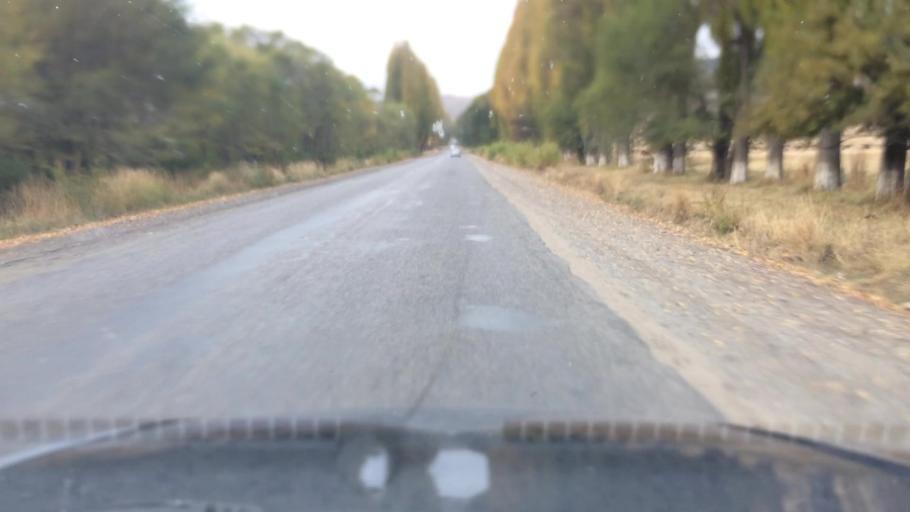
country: KG
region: Ysyk-Koel
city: Pokrovka
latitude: 42.7381
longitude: 77.9209
